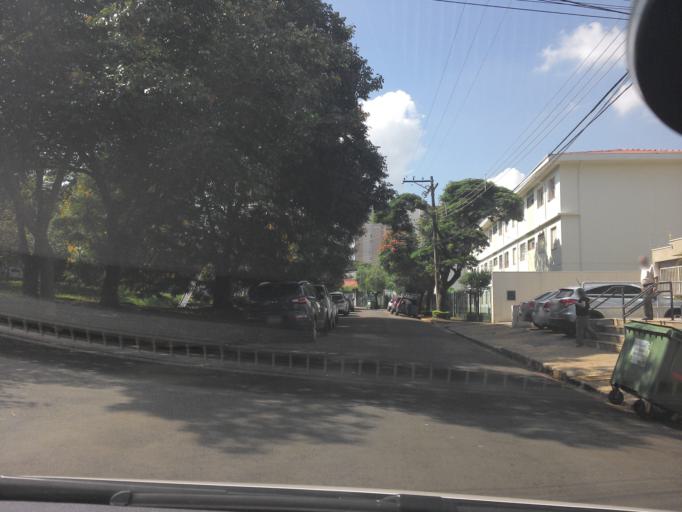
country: BR
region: Sao Paulo
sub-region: Campinas
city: Campinas
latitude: -22.8827
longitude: -47.0707
